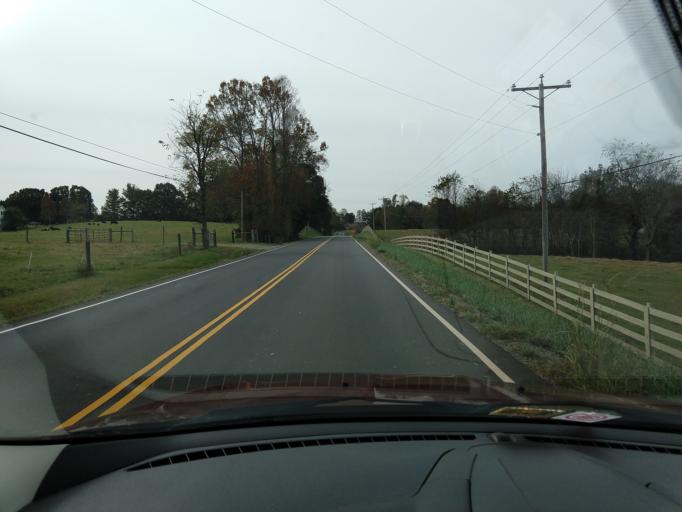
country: US
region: Virginia
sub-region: Franklin County
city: Union Hall
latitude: 36.9857
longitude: -79.7295
